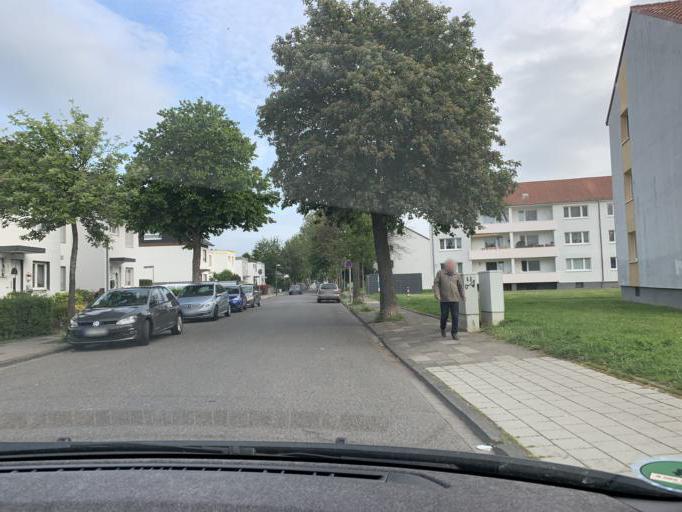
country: DE
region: North Rhine-Westphalia
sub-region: Regierungsbezirk Koln
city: Dueren
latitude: 50.8020
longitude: 6.5022
